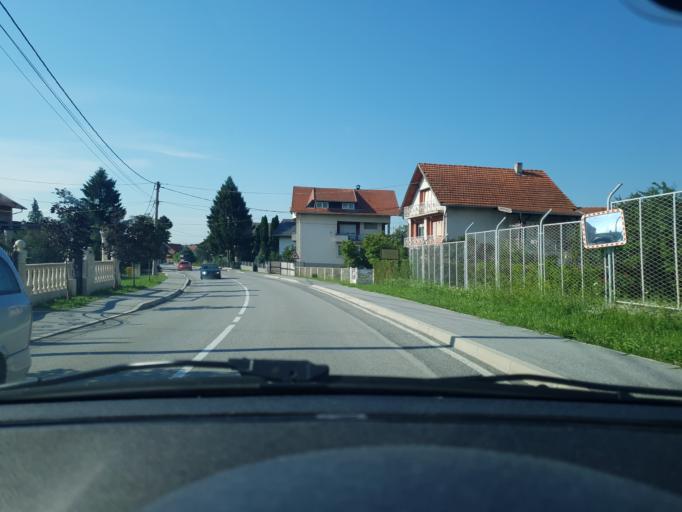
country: HR
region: Zagrebacka
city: Jablanovec
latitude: 45.8892
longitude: 15.8574
